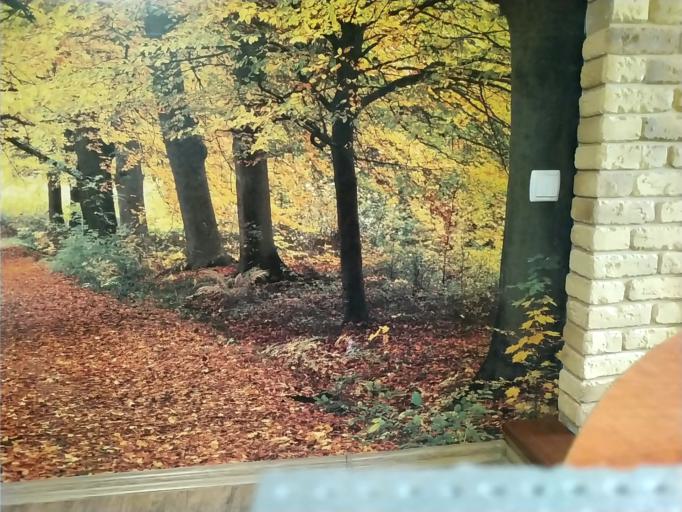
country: RU
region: Tverskaya
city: Staritsa
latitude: 56.5377
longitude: 34.9858
